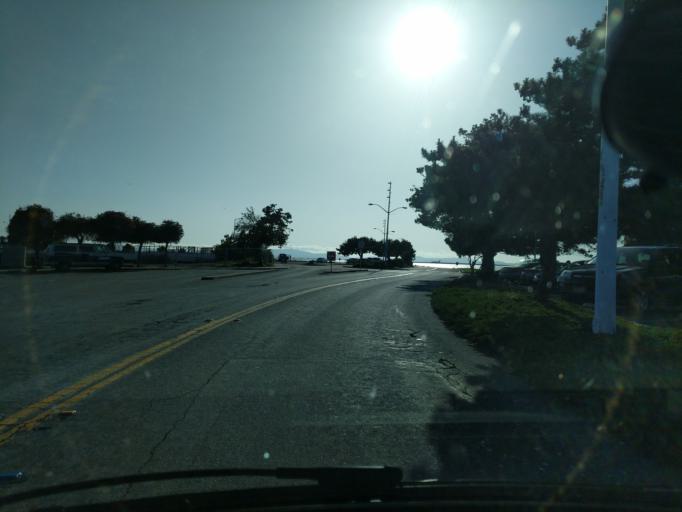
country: US
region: California
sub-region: Alameda County
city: San Leandro
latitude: 37.6985
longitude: -122.1922
